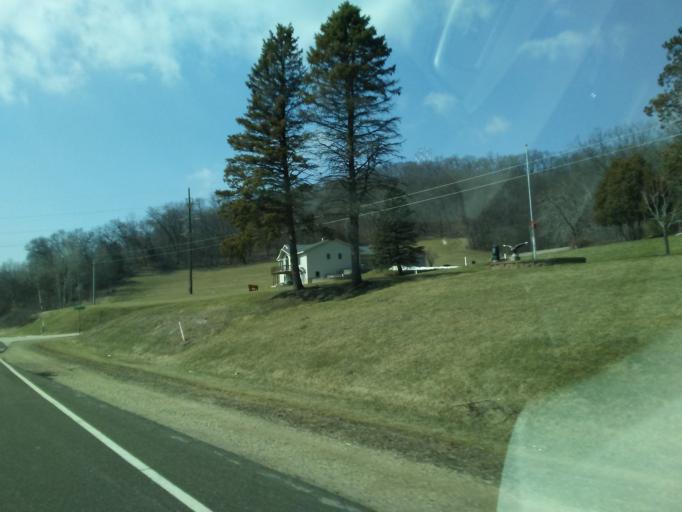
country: US
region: Wisconsin
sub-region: La Crosse County
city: La Crosse
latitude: 43.7666
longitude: -91.1683
